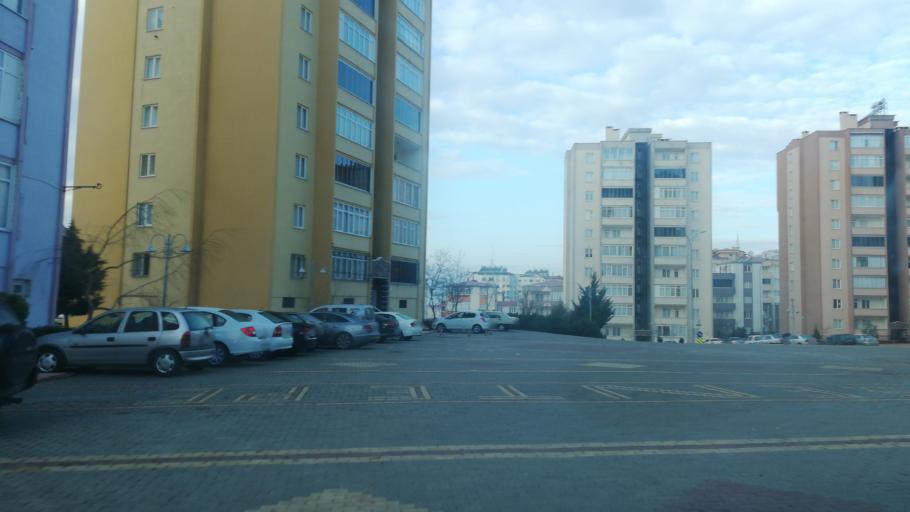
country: TR
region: Kahramanmaras
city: Kahramanmaras
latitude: 37.5950
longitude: 36.9017
